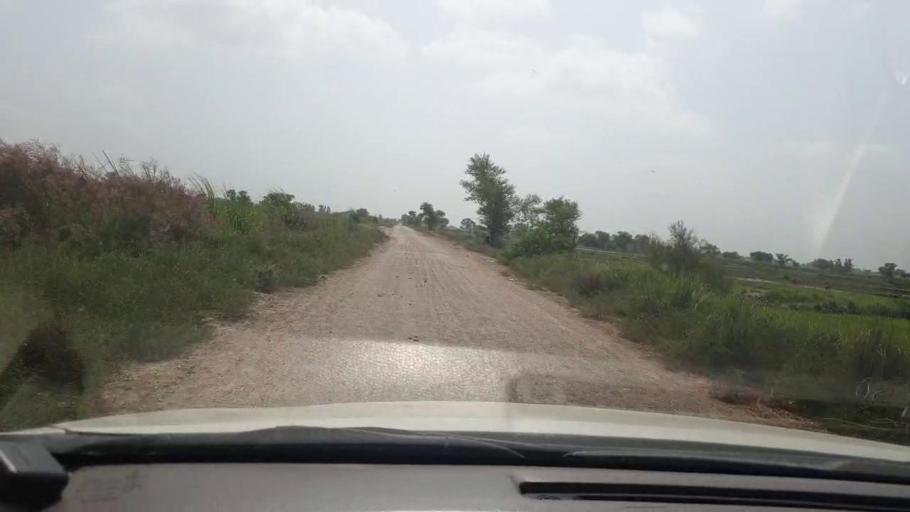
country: PK
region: Sindh
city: Shikarpur
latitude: 28.0112
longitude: 68.5595
